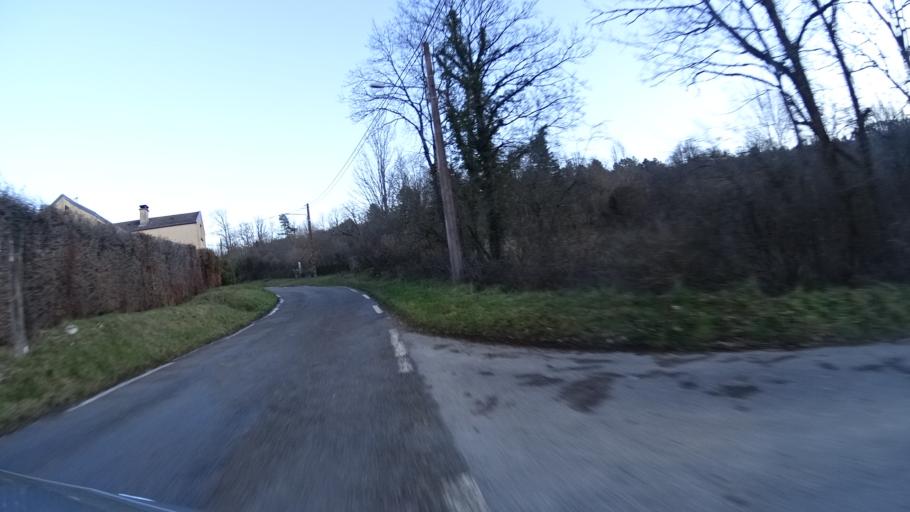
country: FR
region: Franche-Comte
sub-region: Departement du Doubs
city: Besancon
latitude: 47.2233
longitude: 6.0400
